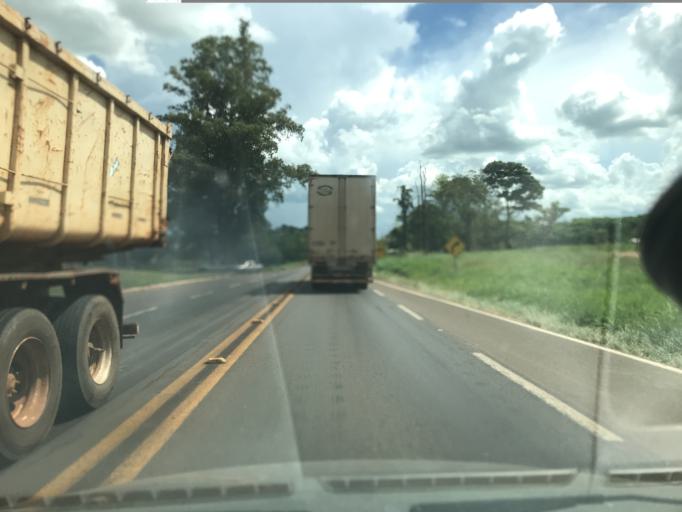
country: BR
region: Parana
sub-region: Cruzeiro Do Oeste
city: Cruzeiro do Oeste
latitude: -23.7958
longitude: -53.0483
